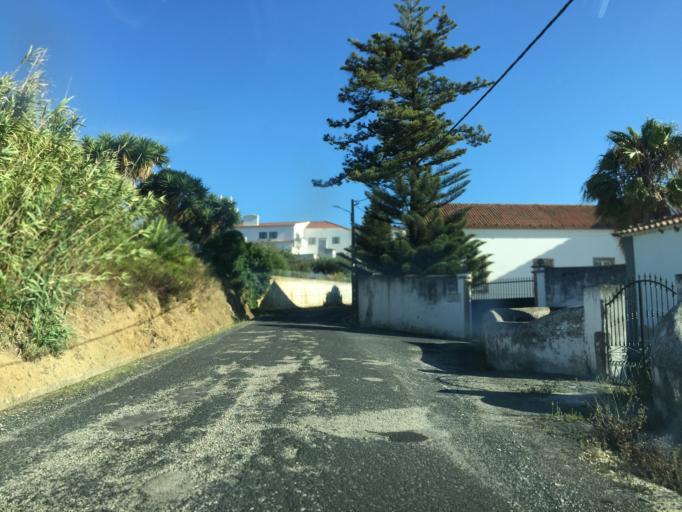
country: PT
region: Lisbon
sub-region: Torres Vedras
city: Torres Vedras
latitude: 39.0914
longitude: -9.2793
